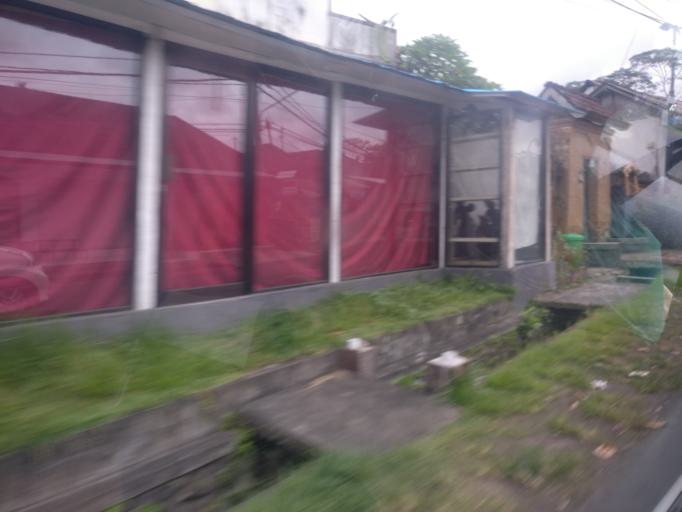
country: ID
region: Bali
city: Banjar Tengah
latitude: -8.4564
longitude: 115.2784
